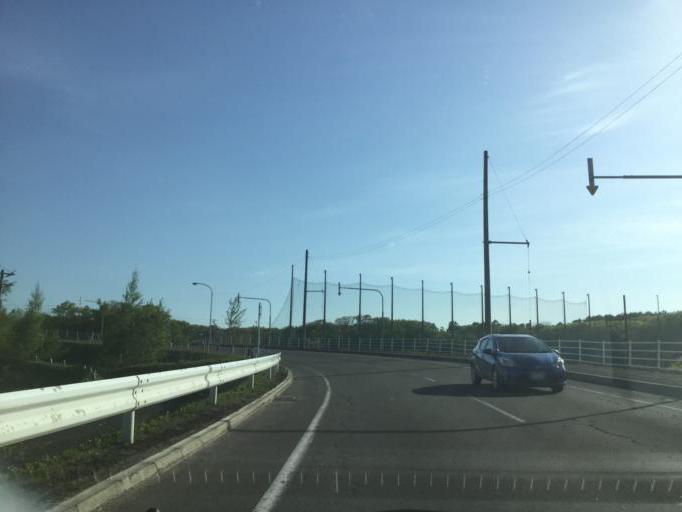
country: JP
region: Hokkaido
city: Kitahiroshima
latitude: 43.0012
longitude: 141.5464
